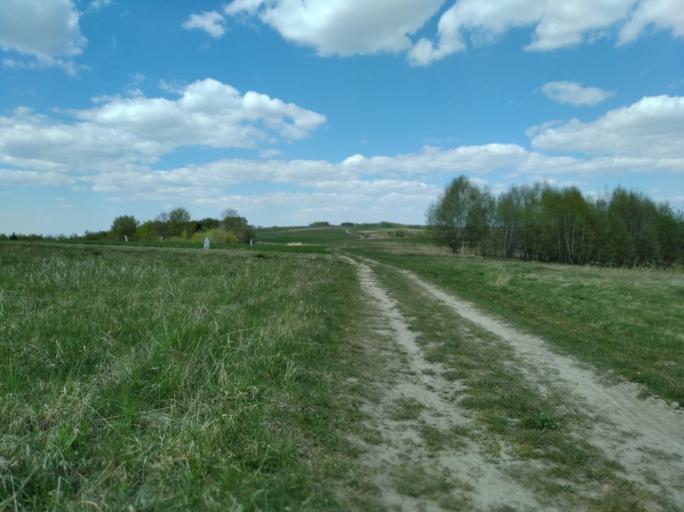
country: PL
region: Subcarpathian Voivodeship
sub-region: Powiat brzozowski
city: Golcowa
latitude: 49.7557
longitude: 22.0717
